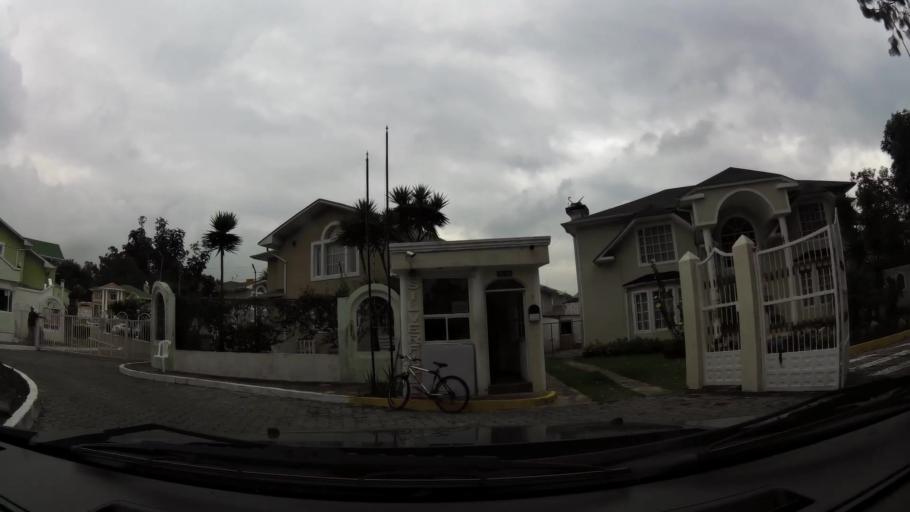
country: EC
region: Pichincha
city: Sangolqui
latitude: -0.3001
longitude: -78.4680
